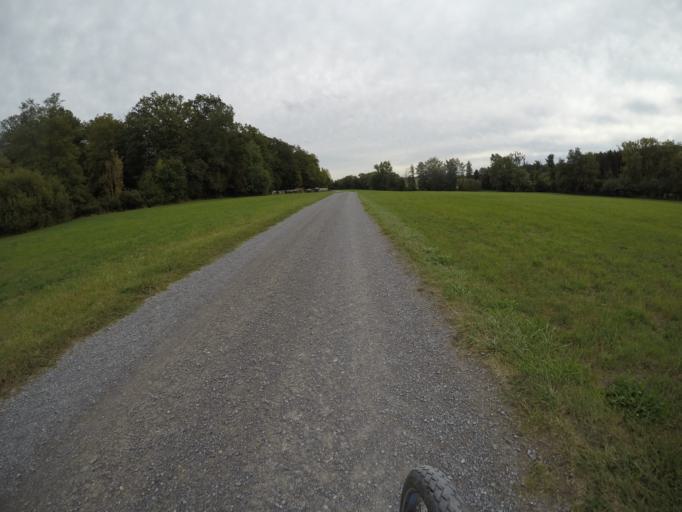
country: DE
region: Baden-Wuerttemberg
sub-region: Karlsruhe Region
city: Illingen
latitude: 48.9682
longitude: 8.8894
